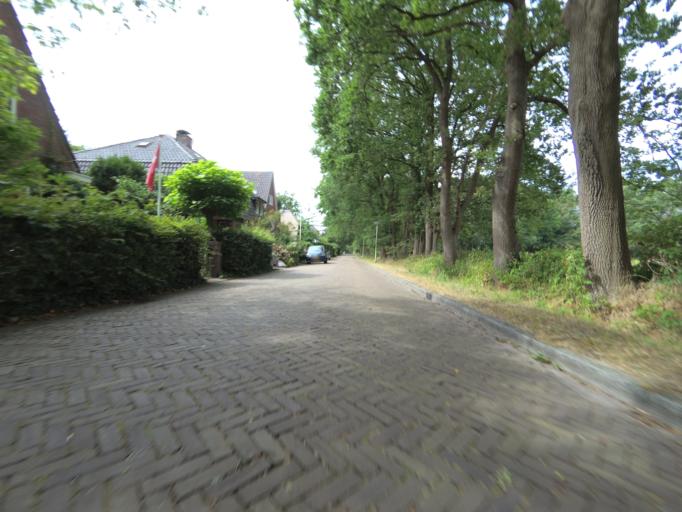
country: NL
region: Overijssel
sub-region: Gemeente Enschede
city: Enschede
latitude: 52.2388
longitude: 6.9205
